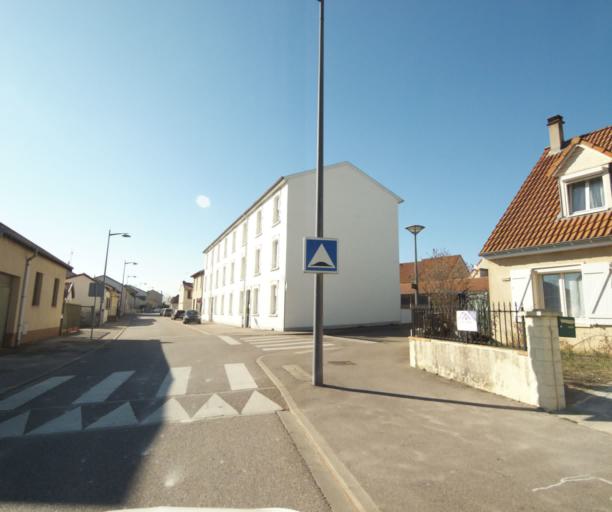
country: FR
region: Lorraine
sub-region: Departement de Meurthe-et-Moselle
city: Tomblaine
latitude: 48.6834
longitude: 6.2194
